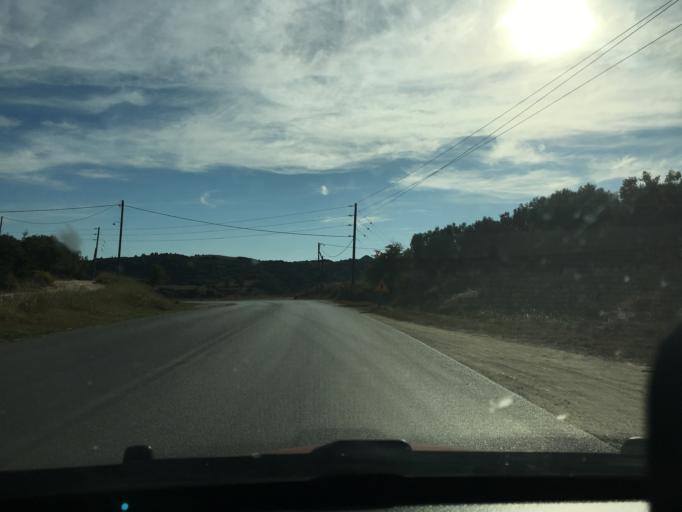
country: GR
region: Central Macedonia
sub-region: Nomos Chalkidikis
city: Agios Nikolaos
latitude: 40.2437
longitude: 23.7075
